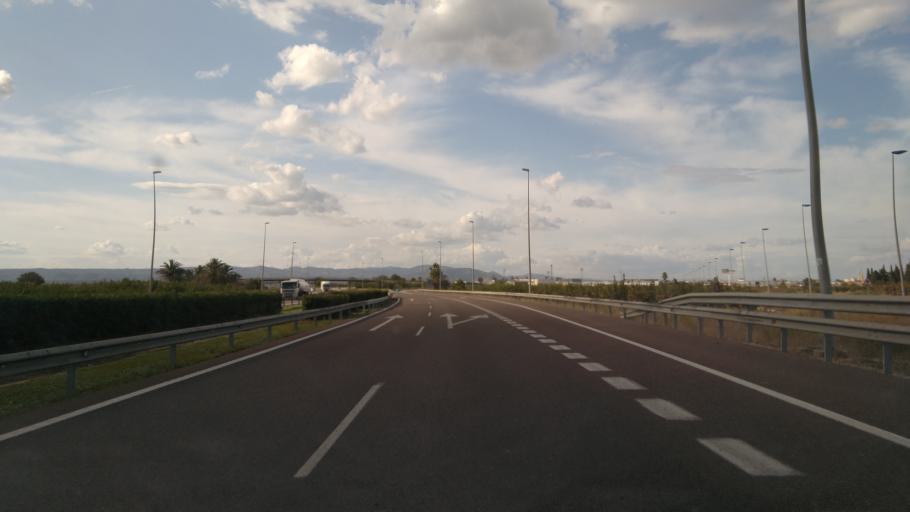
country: ES
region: Valencia
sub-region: Provincia de Valencia
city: Guadassuar
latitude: 39.1759
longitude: -0.4706
